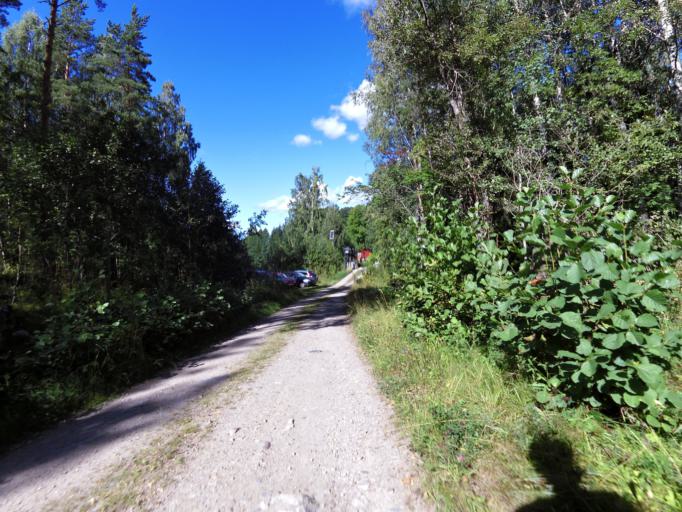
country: SE
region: Gaevleborg
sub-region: Gavle Kommun
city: Valbo
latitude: 60.7529
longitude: 16.9736
